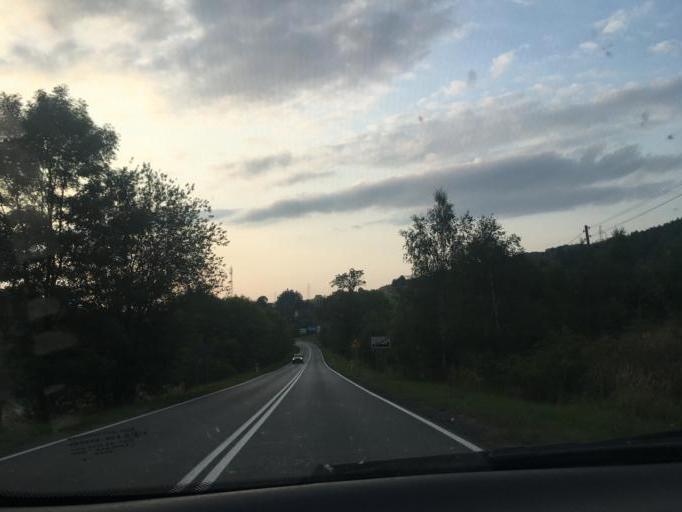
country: PL
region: Lower Silesian Voivodeship
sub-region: Powiat klodzki
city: Bozkow
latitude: 50.5336
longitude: 16.5807
